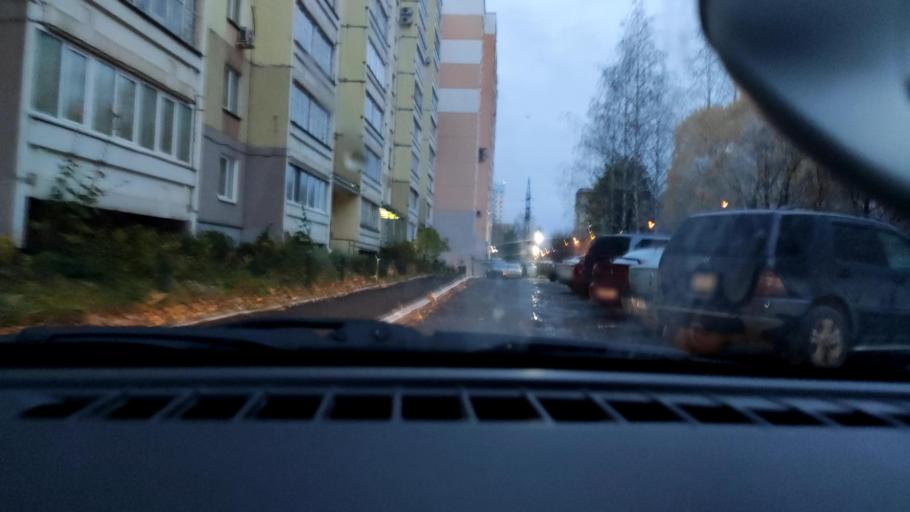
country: RU
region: Perm
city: Perm
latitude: 57.9941
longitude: 56.2255
